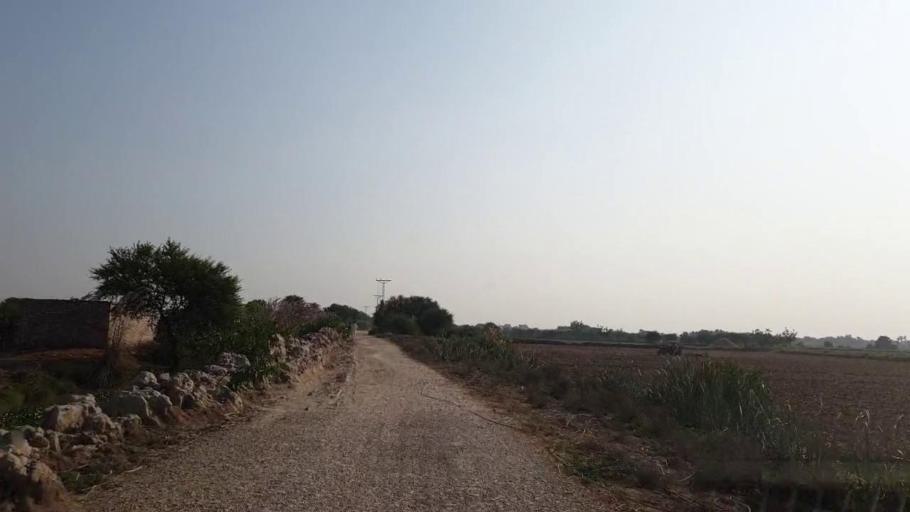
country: PK
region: Sindh
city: Bulri
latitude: 24.9836
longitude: 68.3773
